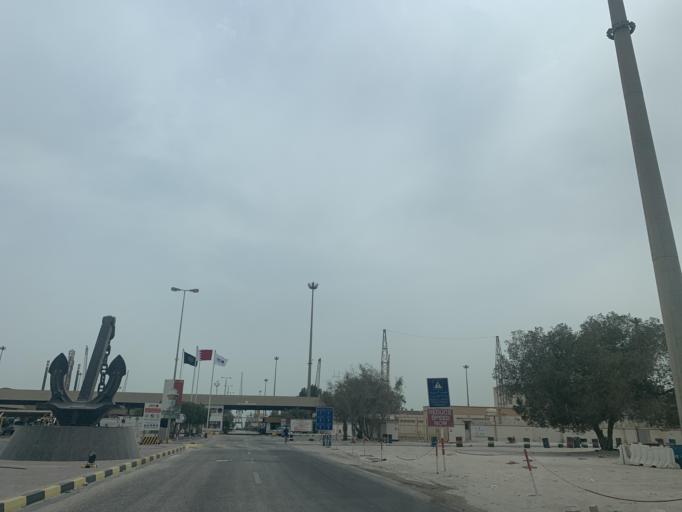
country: BH
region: Muharraq
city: Al Hadd
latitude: 26.1935
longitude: 50.6647
